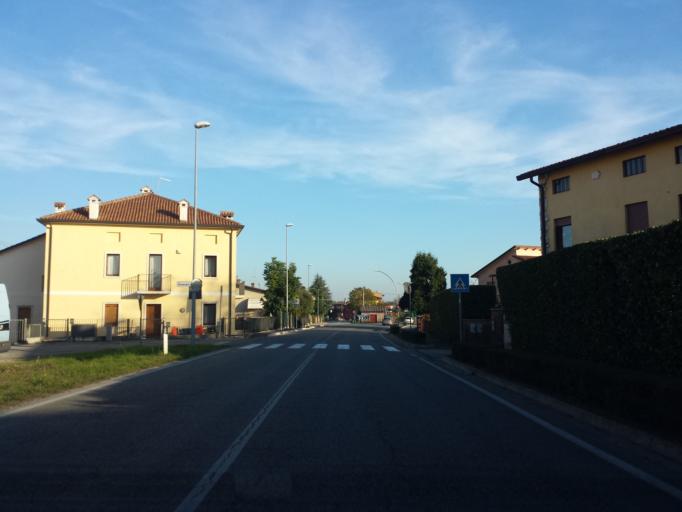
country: IT
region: Veneto
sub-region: Provincia di Vicenza
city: Motta
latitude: 45.6052
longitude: 11.4904
